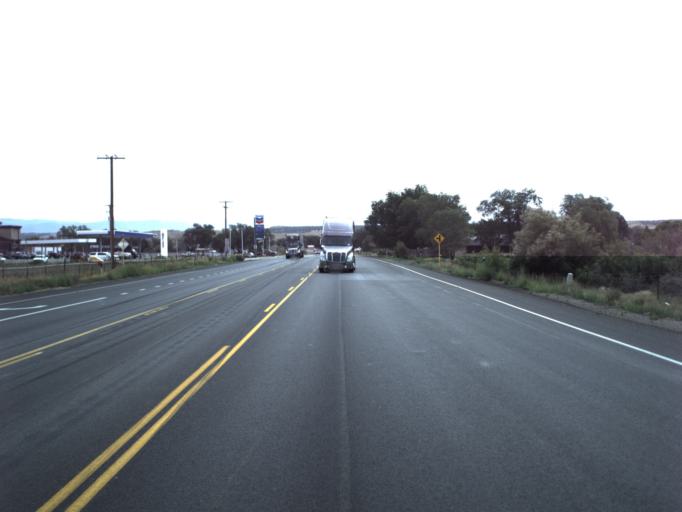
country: US
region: Utah
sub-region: Carbon County
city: Wellington
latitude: 39.5425
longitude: -110.6919
